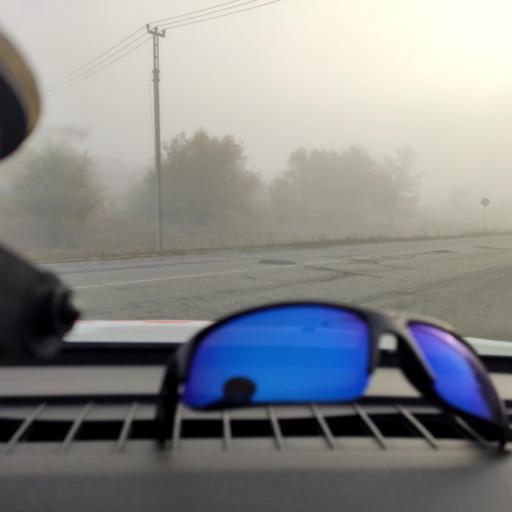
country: RU
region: Samara
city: Chapayevsk
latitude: 53.0056
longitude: 49.7431
